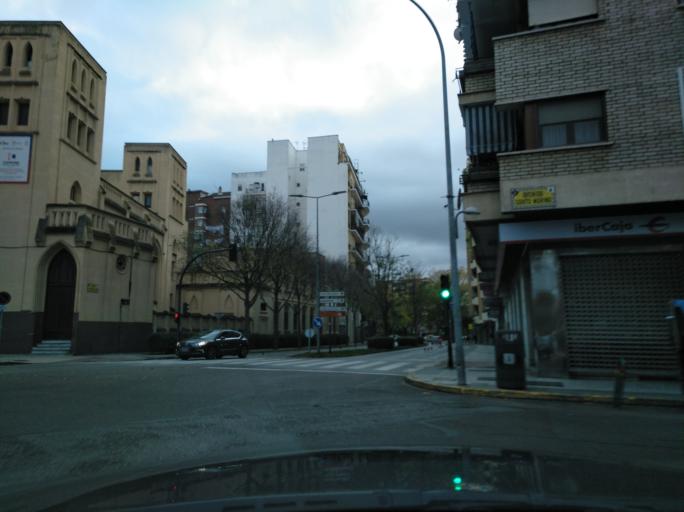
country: ES
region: Extremadura
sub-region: Provincia de Badajoz
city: Badajoz
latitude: 38.8750
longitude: -6.9785
